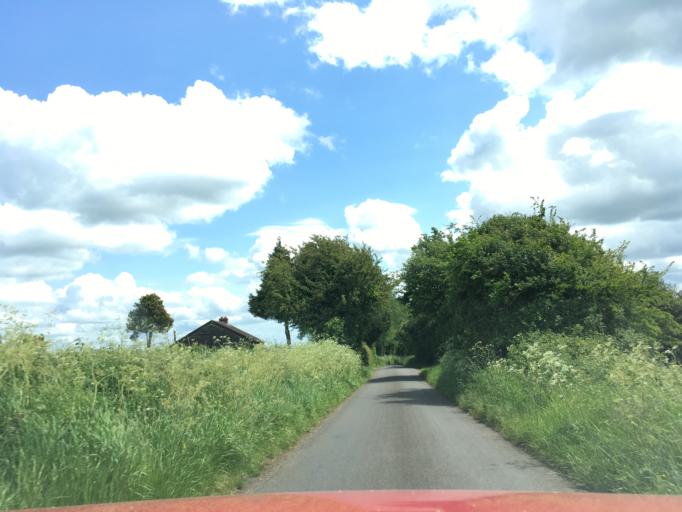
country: GB
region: England
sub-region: Gloucestershire
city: Painswick
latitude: 51.7856
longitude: -2.1398
